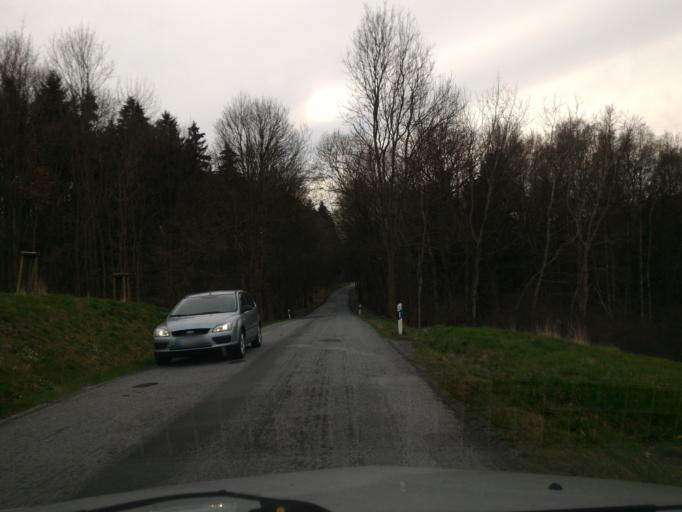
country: DE
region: Saxony
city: Hainewalde
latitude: 50.9225
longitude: 14.7315
